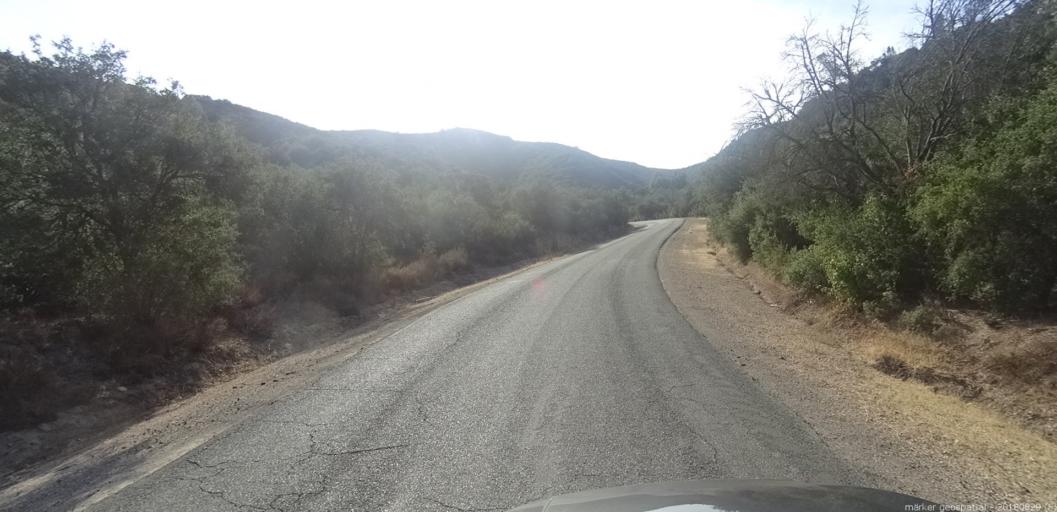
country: US
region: California
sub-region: Monterey County
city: King City
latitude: 36.0284
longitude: -121.0705
